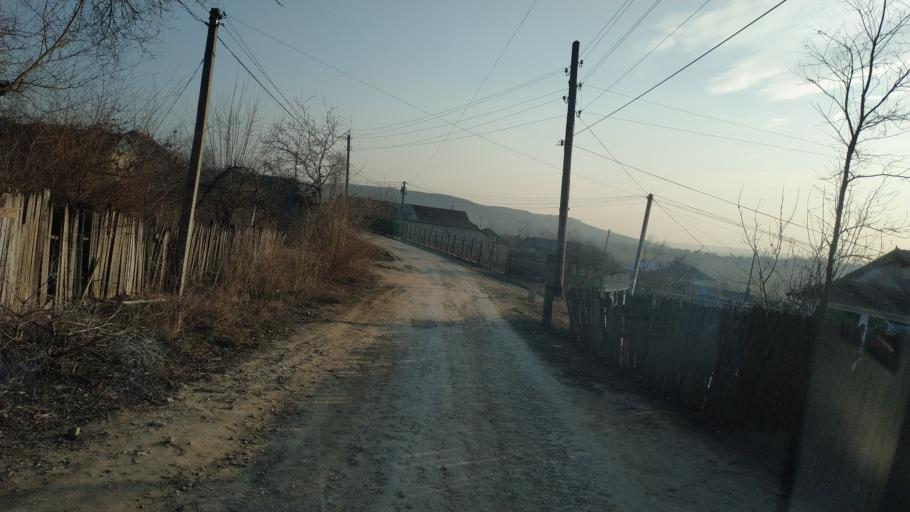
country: MD
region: Hincesti
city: Dancu
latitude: 46.7719
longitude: 28.3539
